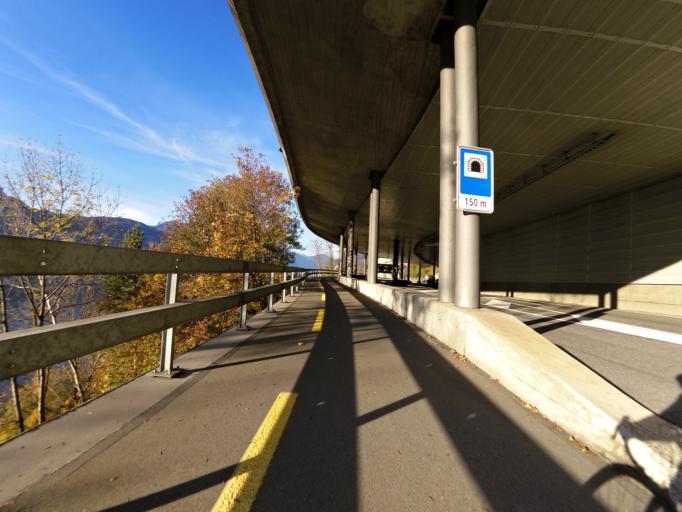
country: CH
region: Uri
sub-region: Uri
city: Flueelen
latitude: 46.9304
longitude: 8.6131
